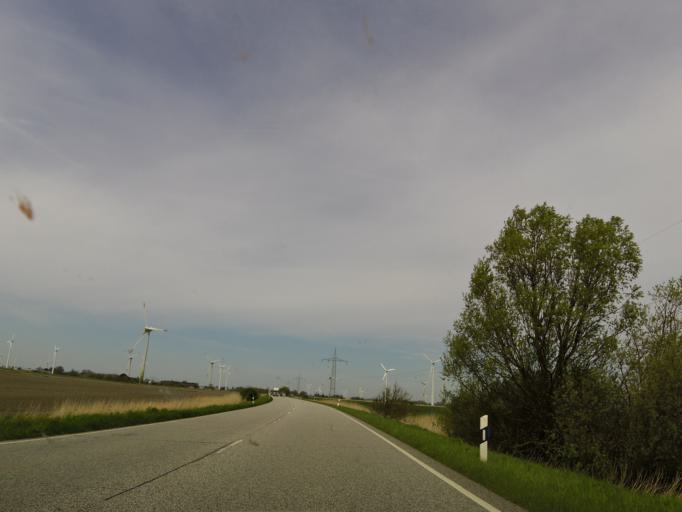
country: DE
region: Schleswig-Holstein
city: Stelle-Wittenwurth
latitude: 54.2624
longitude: 9.0330
